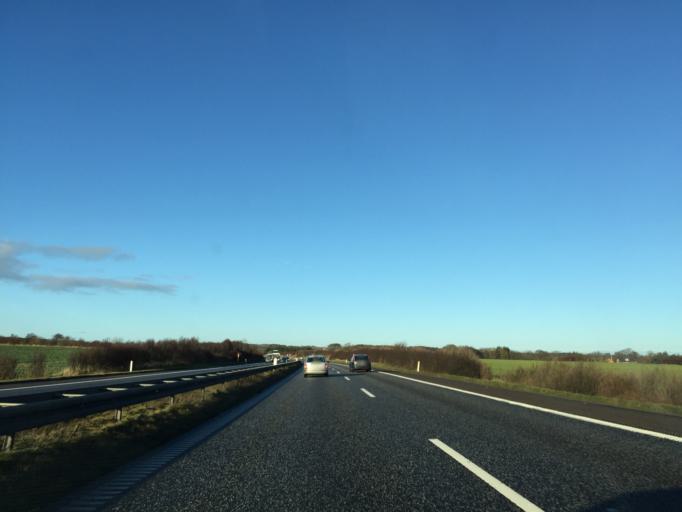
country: DK
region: South Denmark
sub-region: Fredericia Kommune
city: Taulov
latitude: 55.5808
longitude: 9.6124
